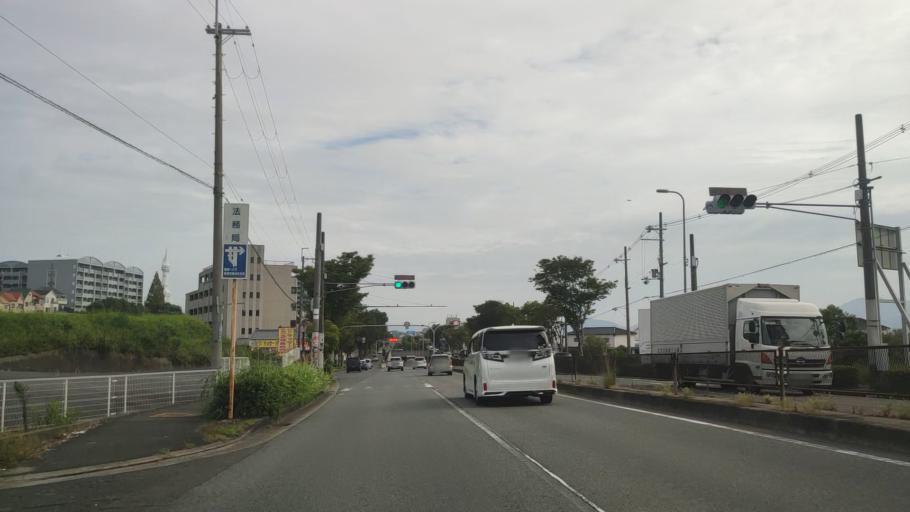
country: JP
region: Osaka
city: Tondabayashicho
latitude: 34.4887
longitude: 135.5826
